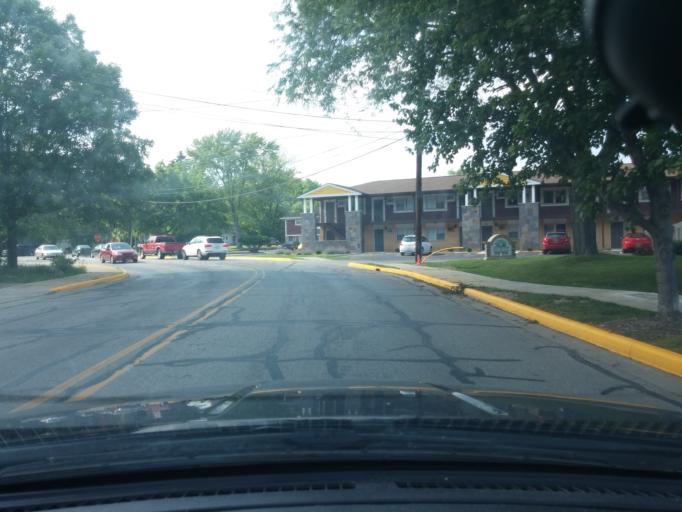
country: US
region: Indiana
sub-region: Tippecanoe County
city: West Lafayette
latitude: 40.4346
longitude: -86.9050
